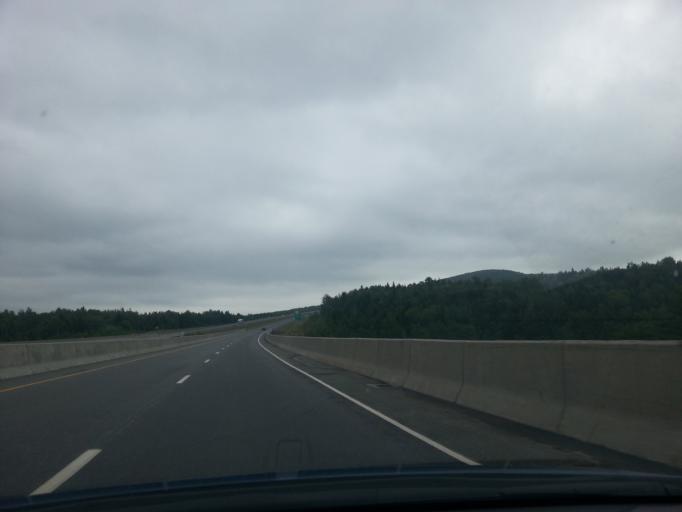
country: CA
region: New Brunswick
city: Nackawic
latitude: 45.9931
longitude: -67.4999
